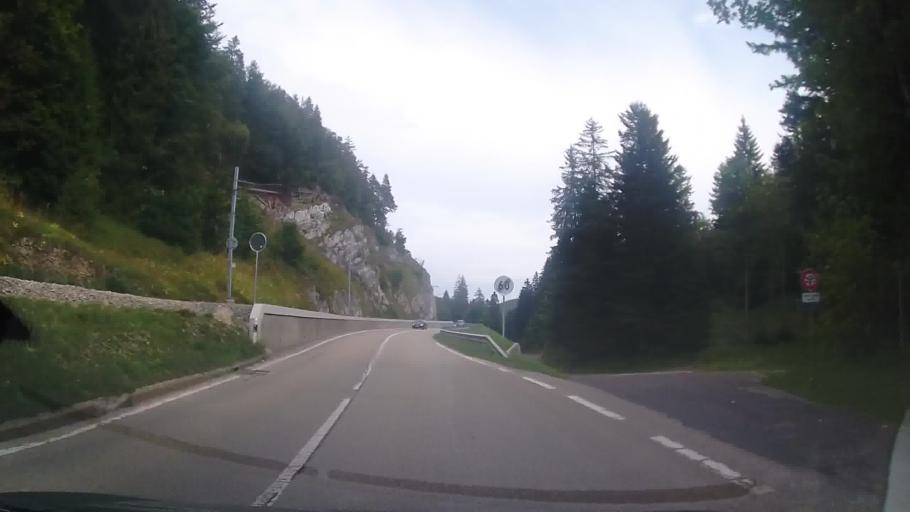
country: CH
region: Vaud
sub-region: Nyon District
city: Saint-Cergue
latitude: 46.4505
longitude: 6.1284
